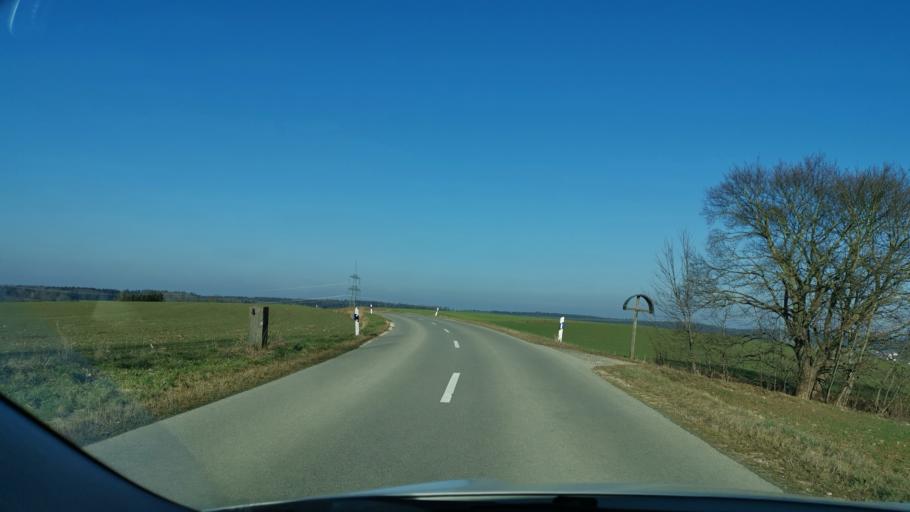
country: DE
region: Bavaria
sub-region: Swabia
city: Aindling
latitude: 48.5210
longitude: 10.9527
